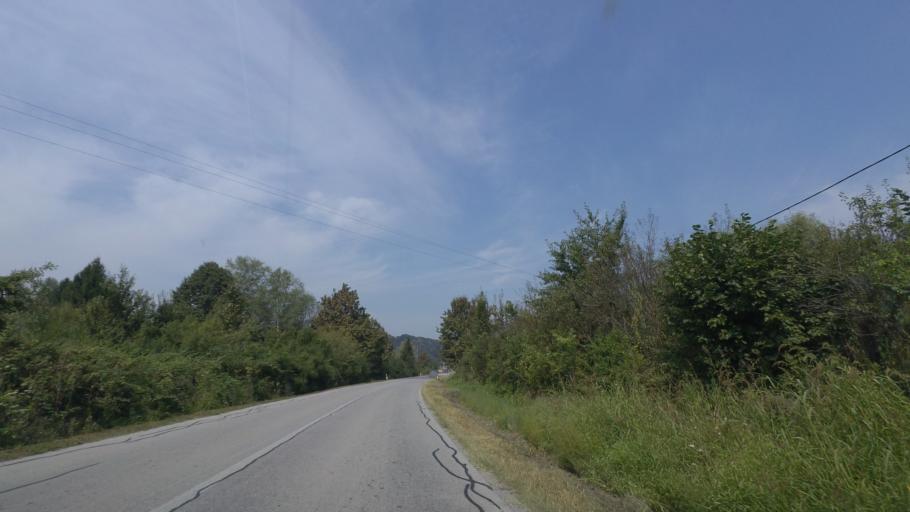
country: HR
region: Sisacko-Moslavacka
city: Glina
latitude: 45.3055
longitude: 16.1212
